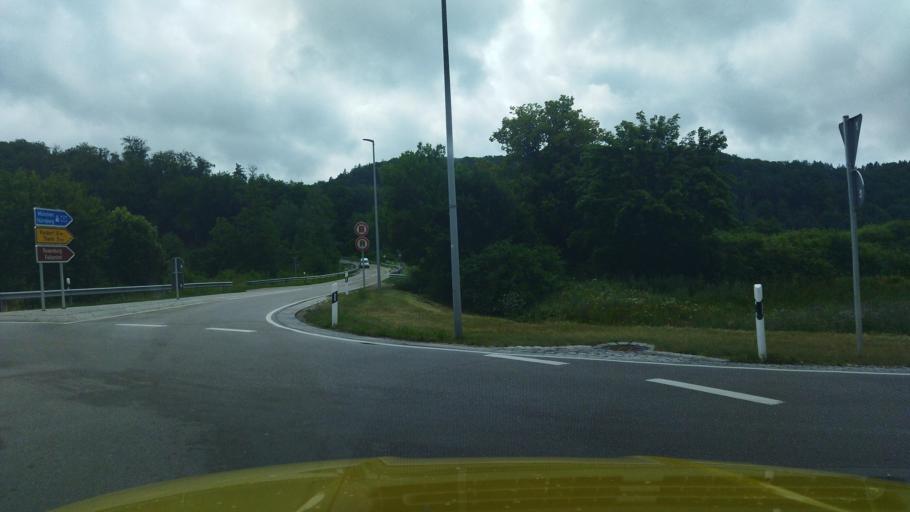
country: DE
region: Bavaria
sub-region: Lower Bavaria
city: Riedenburg
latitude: 48.9467
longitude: 11.6875
